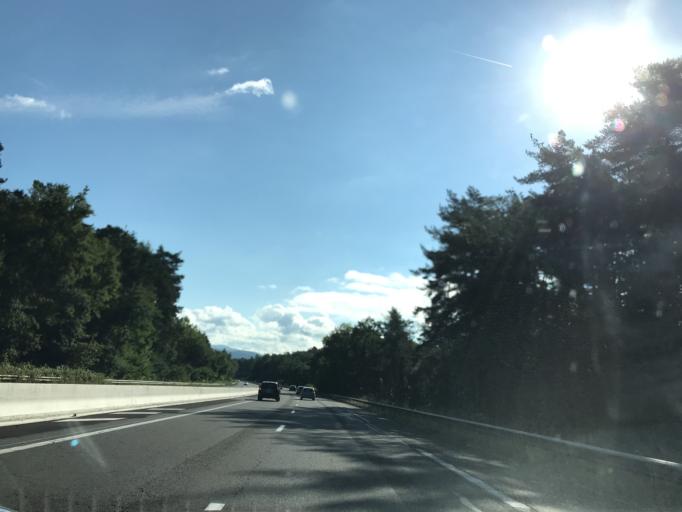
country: FR
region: Auvergne
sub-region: Departement du Puy-de-Dome
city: Orleat
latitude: 45.8494
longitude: 3.4443
